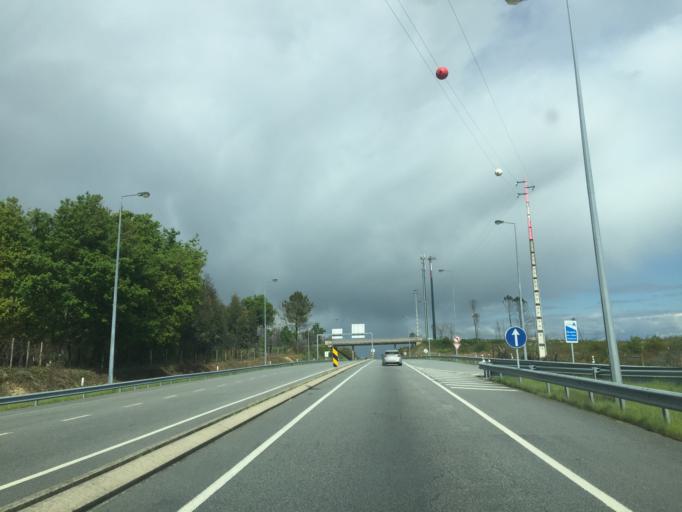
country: PT
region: Viseu
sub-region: Vouzela
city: Vouzela
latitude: 40.6458
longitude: -8.0594
